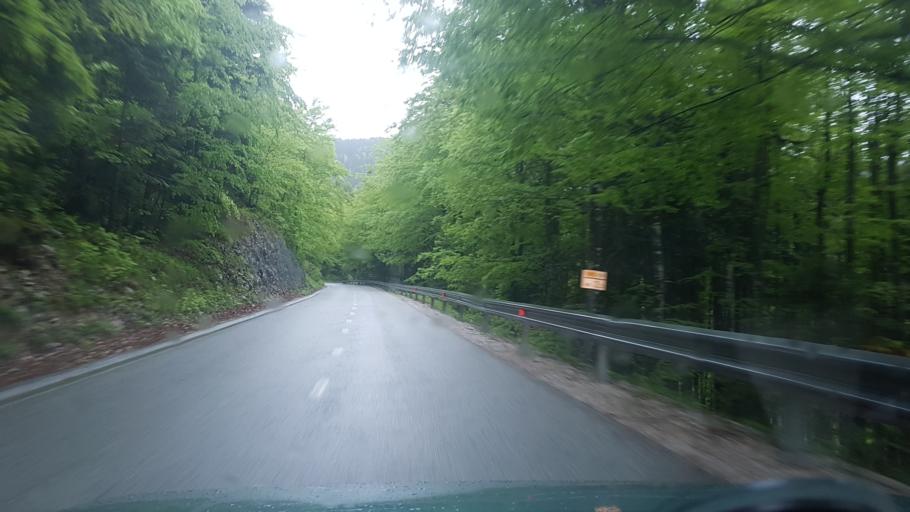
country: SI
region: Bohinj
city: Bohinjska Bistrica
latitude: 46.2585
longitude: 14.0076
